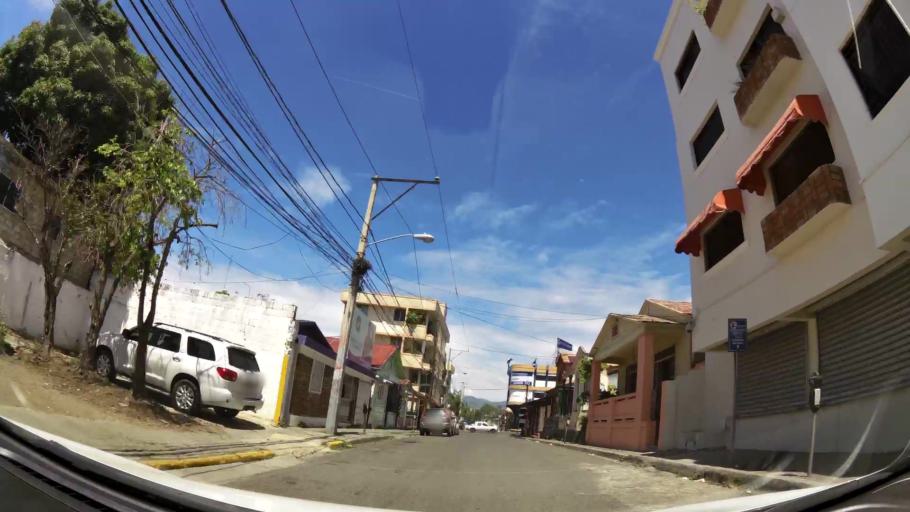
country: DO
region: Santiago
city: Santiago de los Caballeros
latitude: 19.4525
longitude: -70.6968
